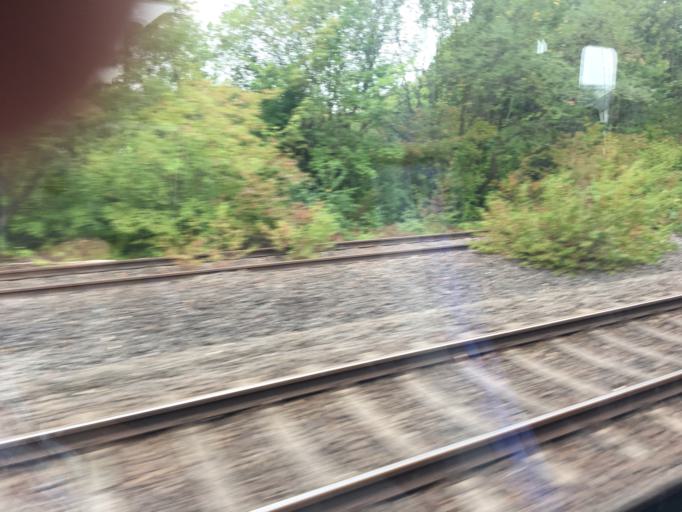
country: DE
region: North Rhine-Westphalia
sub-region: Regierungsbezirk Arnsberg
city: Dortmund
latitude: 51.5091
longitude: 7.4256
